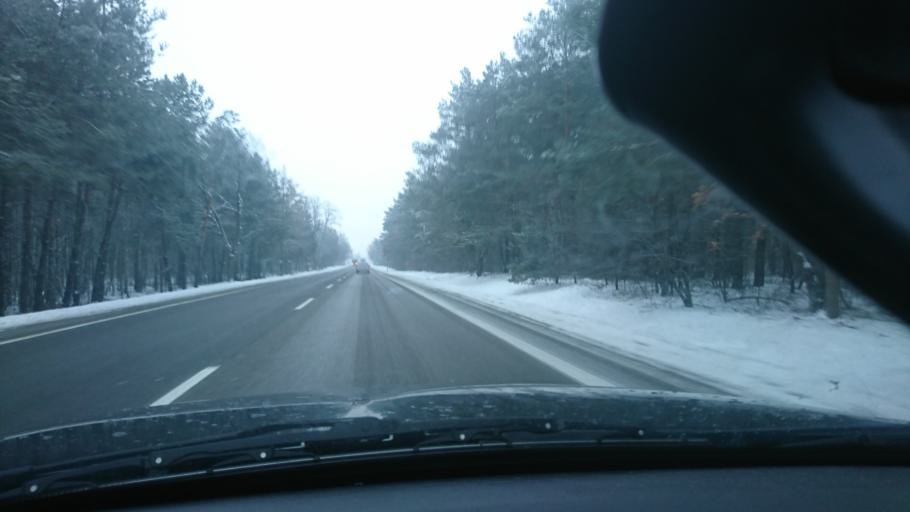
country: PL
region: Masovian Voivodeship
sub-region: Powiat ciechanowski
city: Glinojeck
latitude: 52.8550
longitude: 20.2852
